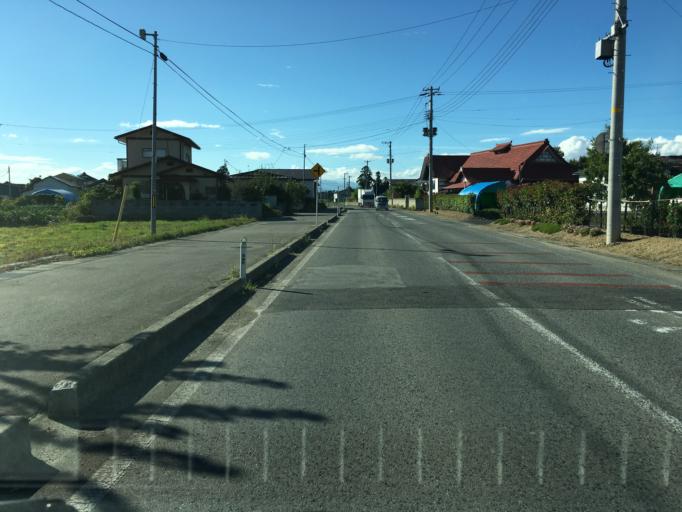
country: JP
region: Yamagata
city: Takahata
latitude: 37.9732
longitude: 140.1628
